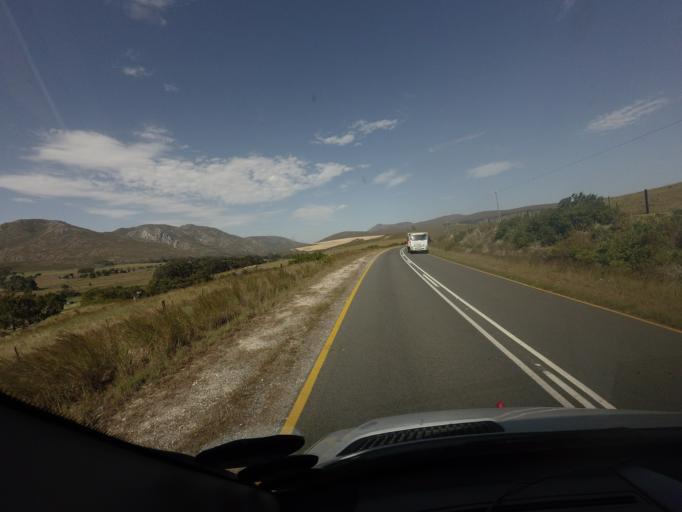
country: ZA
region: Western Cape
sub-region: Overberg District Municipality
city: Caledon
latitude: -34.4190
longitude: 19.5331
